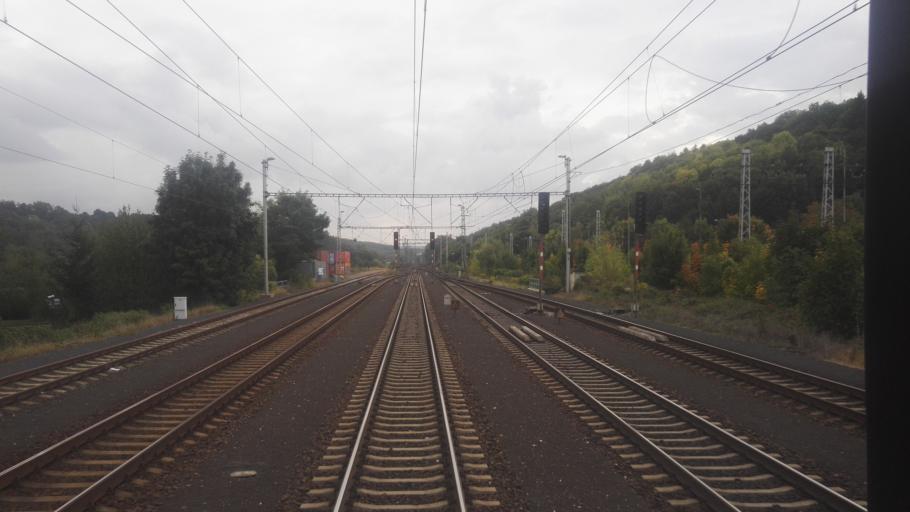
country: CZ
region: Central Bohemia
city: Roztoky
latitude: 50.1554
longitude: 14.3981
